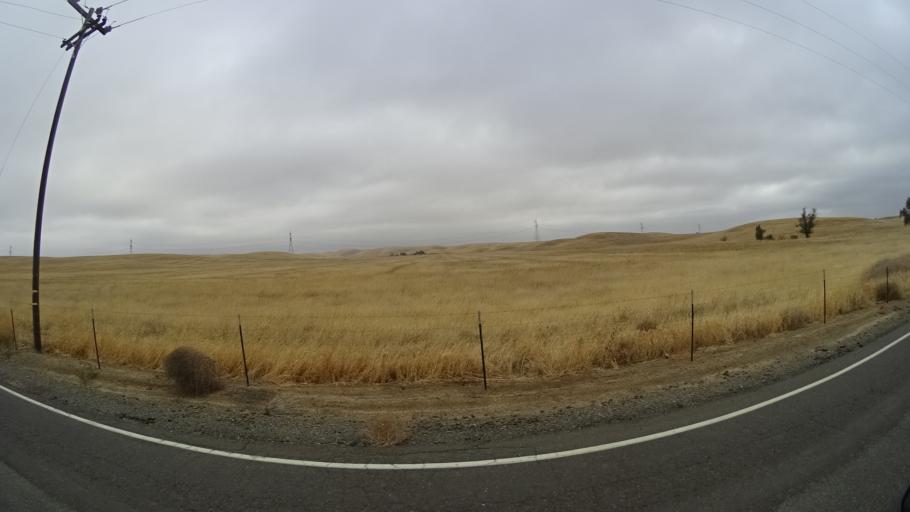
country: US
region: California
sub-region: Yolo County
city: Dunnigan
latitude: 38.8289
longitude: -122.0436
